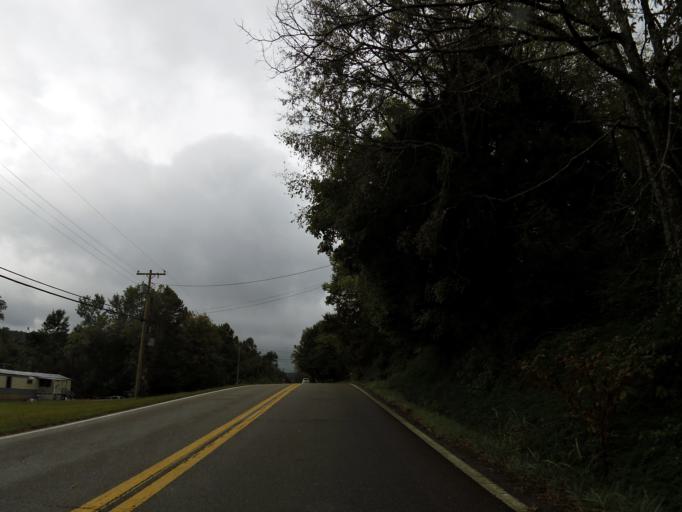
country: US
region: Tennessee
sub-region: Bradley County
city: Cleveland
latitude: 35.1796
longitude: -84.9271
